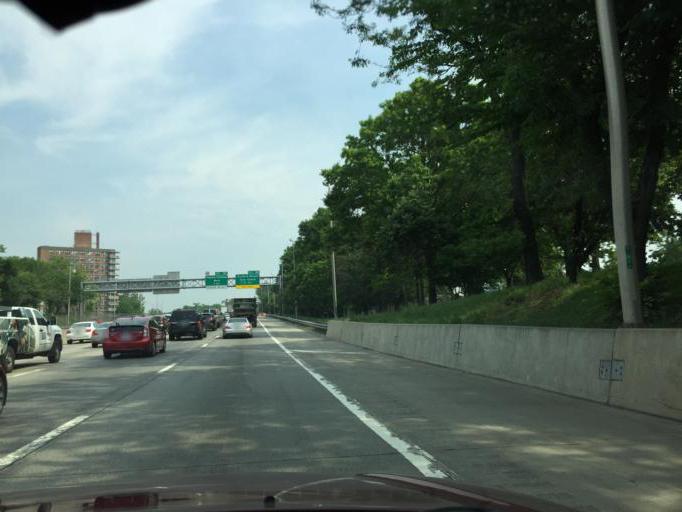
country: US
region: New York
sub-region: Bronx
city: The Bronx
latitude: 40.8430
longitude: -73.8255
